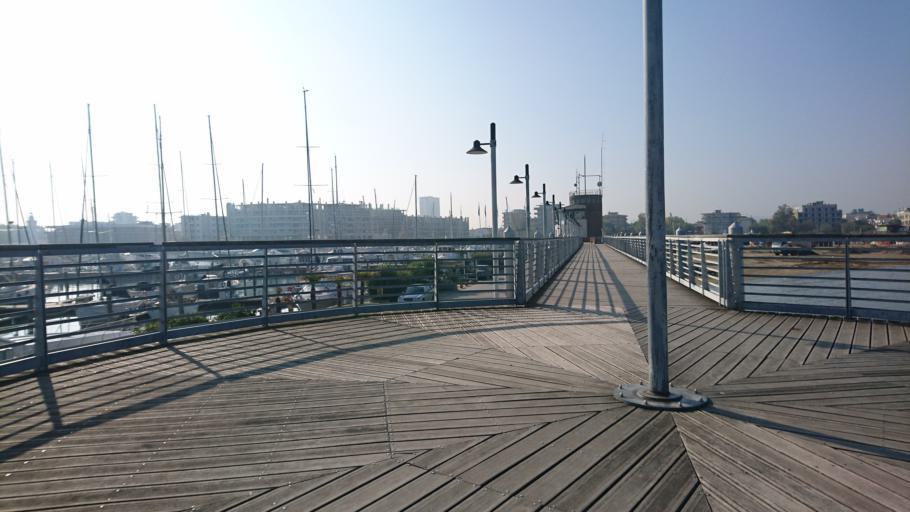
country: IT
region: Emilia-Romagna
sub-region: Provincia di Rimini
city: Rimini
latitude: 44.0773
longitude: 12.5701
